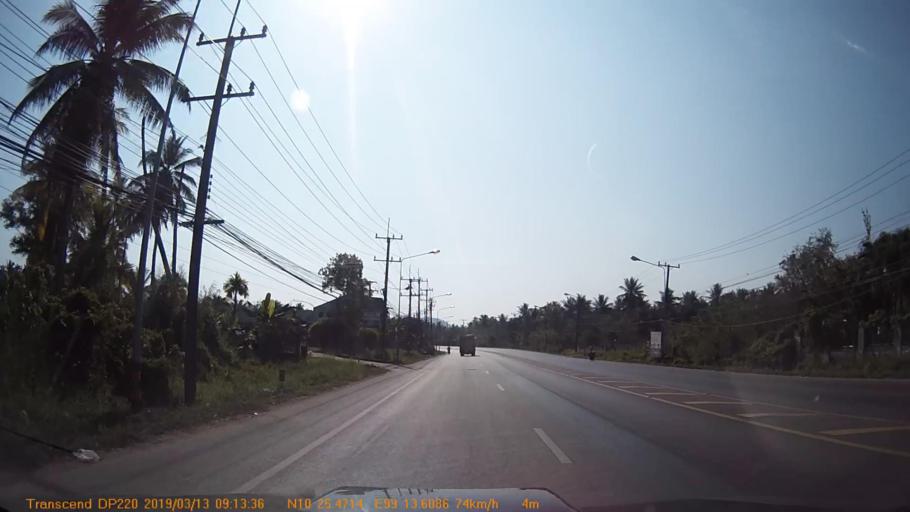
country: TH
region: Chumphon
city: Chumphon
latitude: 10.4244
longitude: 99.2271
